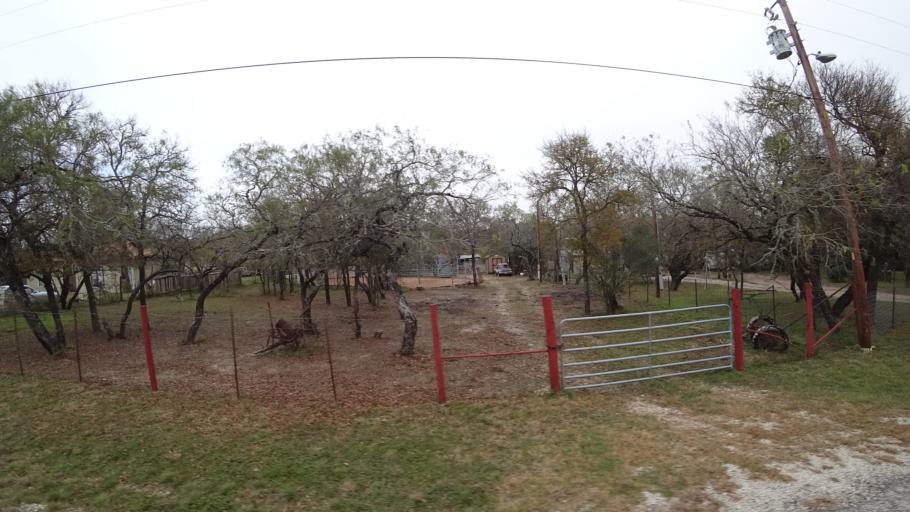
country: US
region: Texas
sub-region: Travis County
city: Garfield
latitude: 30.1015
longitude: -97.5720
